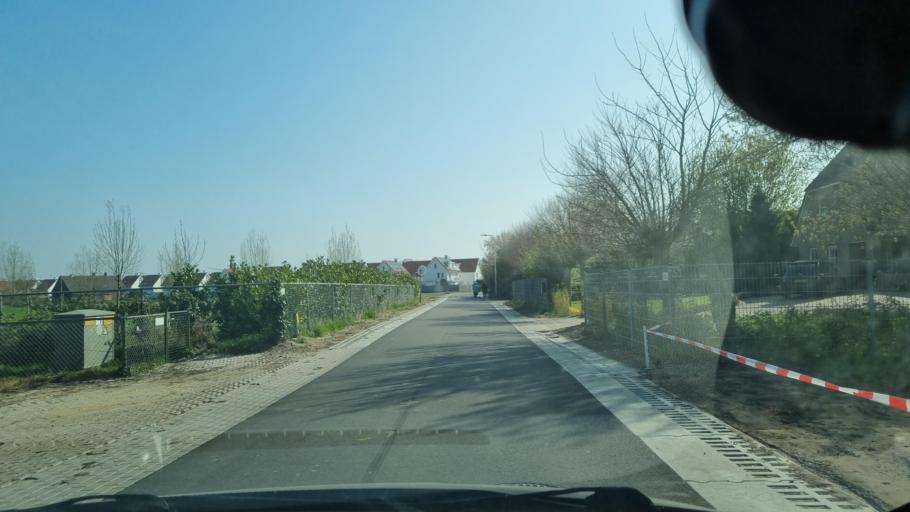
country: NL
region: Gelderland
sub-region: Gemeente Maasdriel
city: Hedel
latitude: 51.7451
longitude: 5.2458
